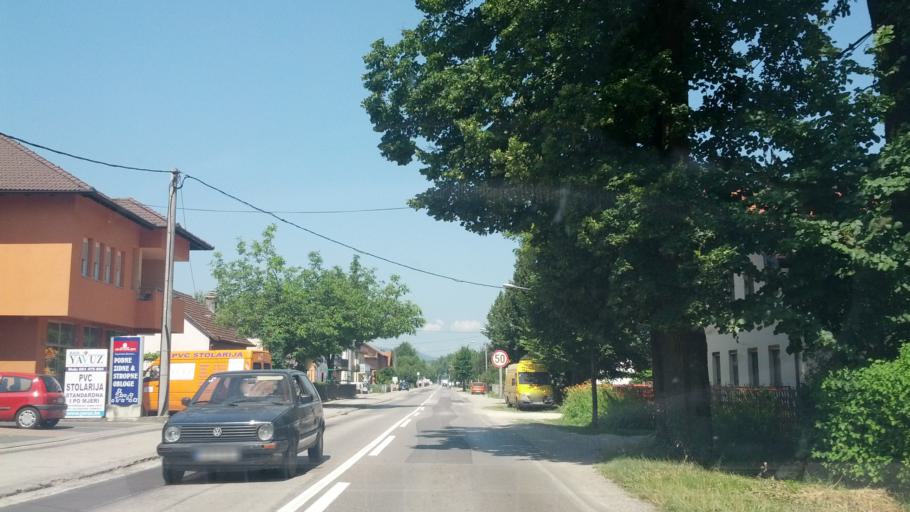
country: BA
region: Federation of Bosnia and Herzegovina
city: Bihac
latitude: 44.8243
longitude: 15.8489
